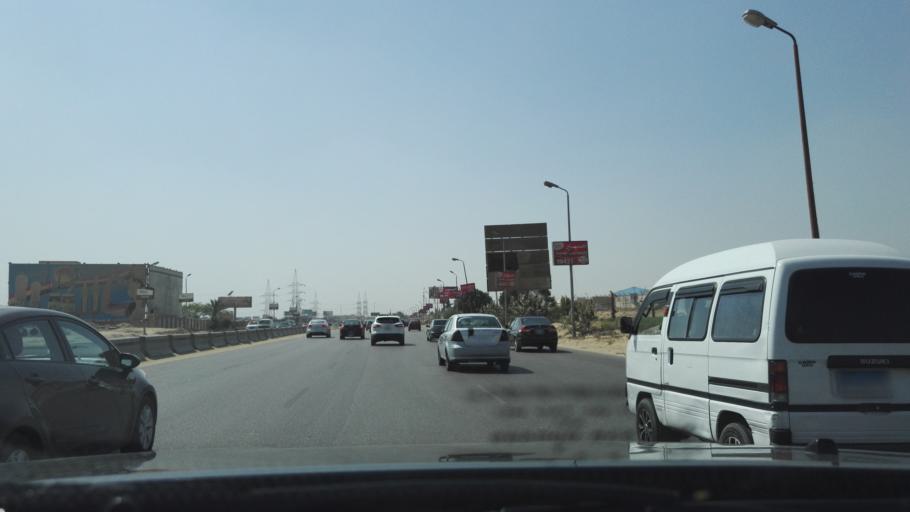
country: EG
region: Muhafazat al Qalyubiyah
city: Al Khankah
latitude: 30.0796
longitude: 31.4207
